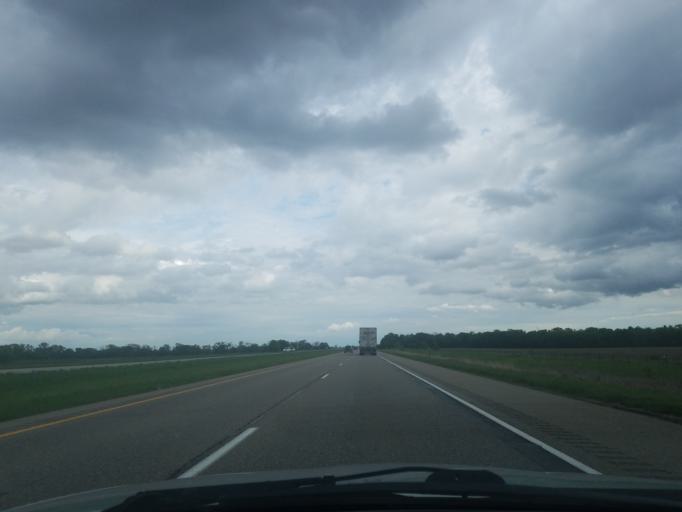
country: US
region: Minnesota
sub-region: Clay County
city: Glyndon
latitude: 46.8386
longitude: -96.6270
